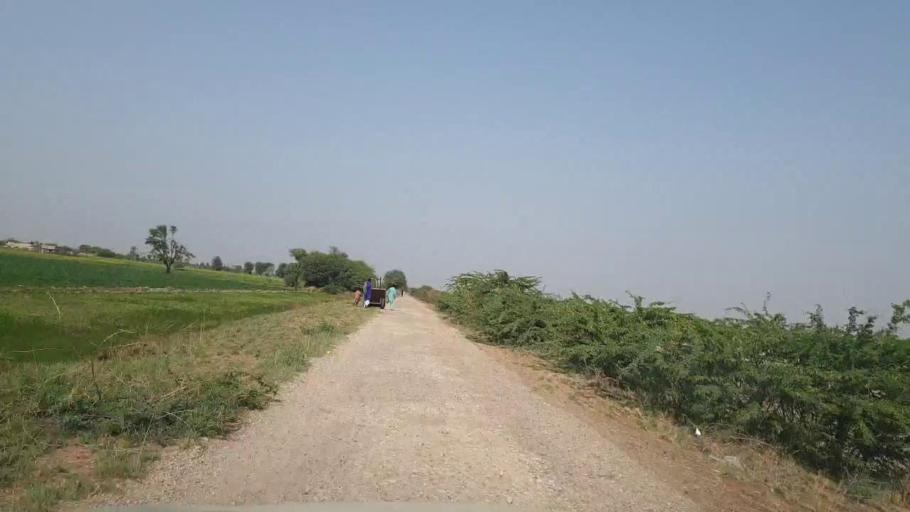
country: PK
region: Sindh
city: Dhoro Naro
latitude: 25.4880
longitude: 69.5819
